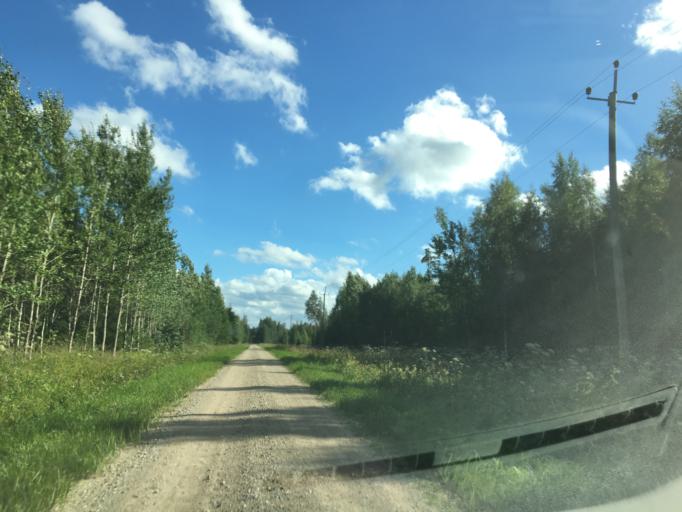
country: EE
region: Viljandimaa
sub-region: Suure-Jaani vald
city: Suure-Jaani
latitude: 58.5370
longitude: 25.2856
